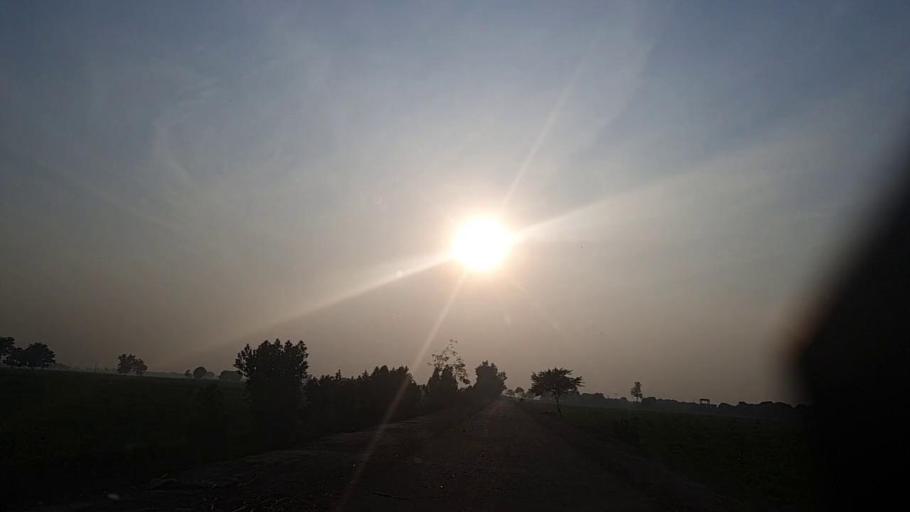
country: PK
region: Sindh
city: Sakrand
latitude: 26.1228
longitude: 68.2298
